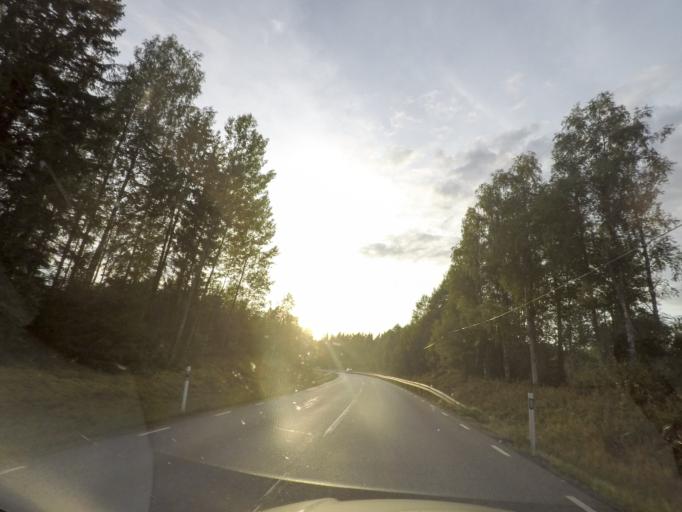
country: SE
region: OErebro
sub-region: Nora Kommun
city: As
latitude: 59.5214
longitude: 14.9004
